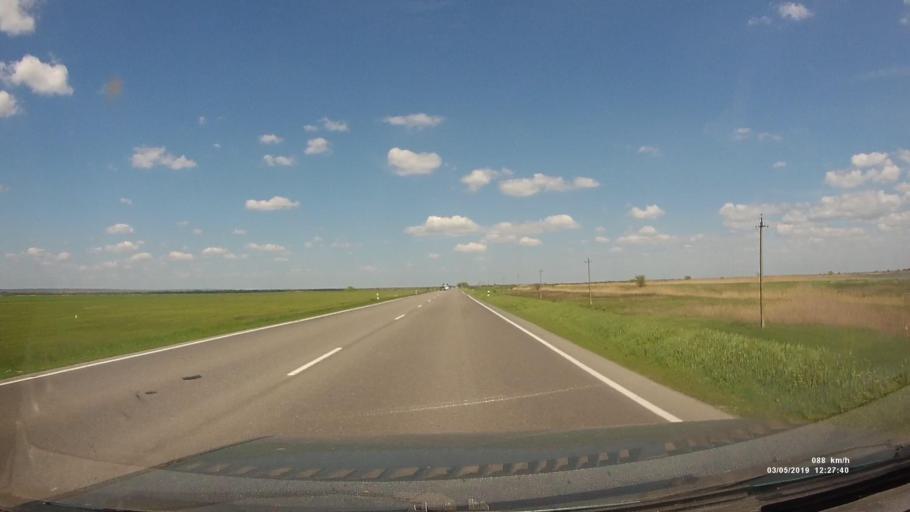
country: RU
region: Rostov
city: Semikarakorsk
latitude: 47.4621
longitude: 40.7226
